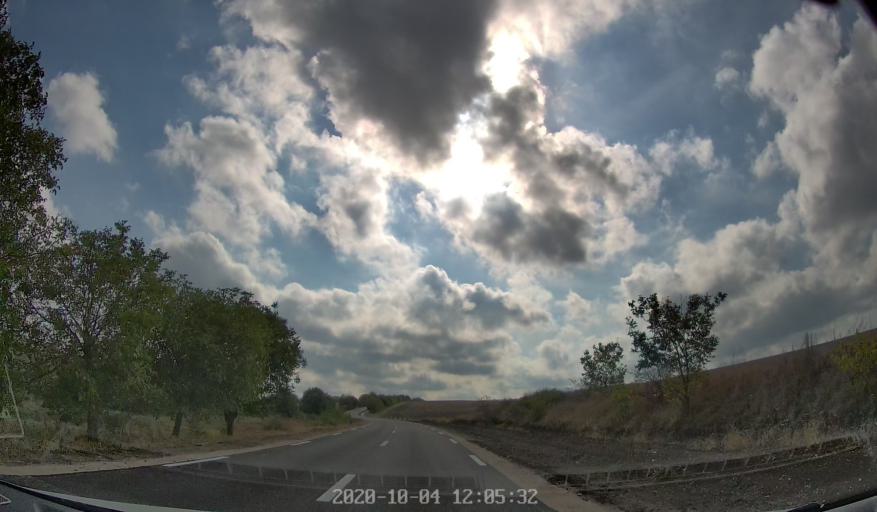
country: MD
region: Rezina
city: Saharna
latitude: 47.5930
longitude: 28.9508
